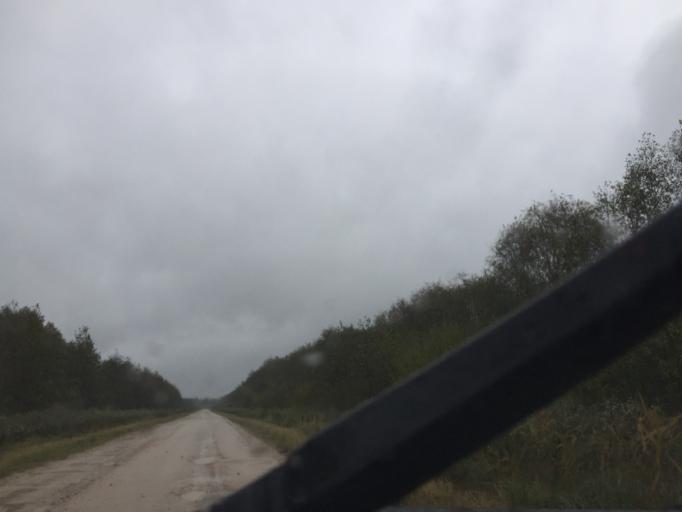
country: LV
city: Tireli
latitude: 56.7472
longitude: 23.5284
